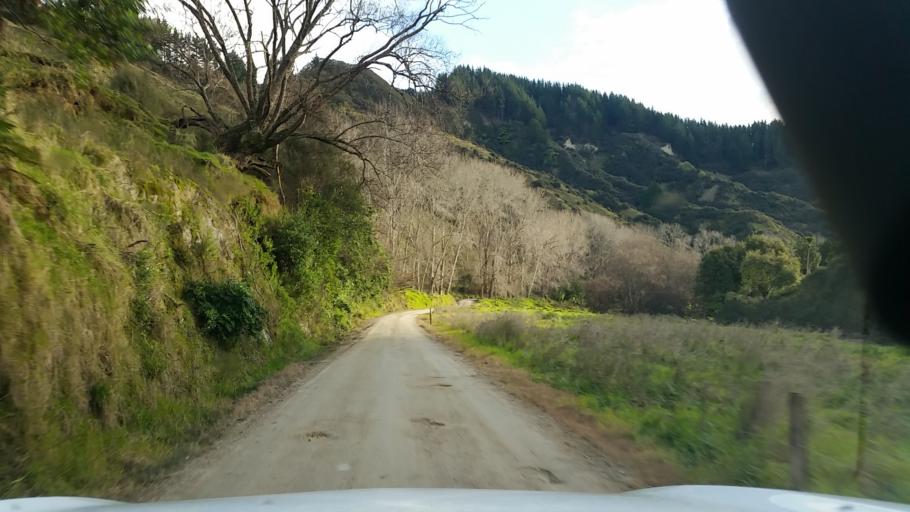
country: NZ
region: Taranaki
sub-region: South Taranaki District
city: Patea
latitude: -39.5720
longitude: 174.8176
